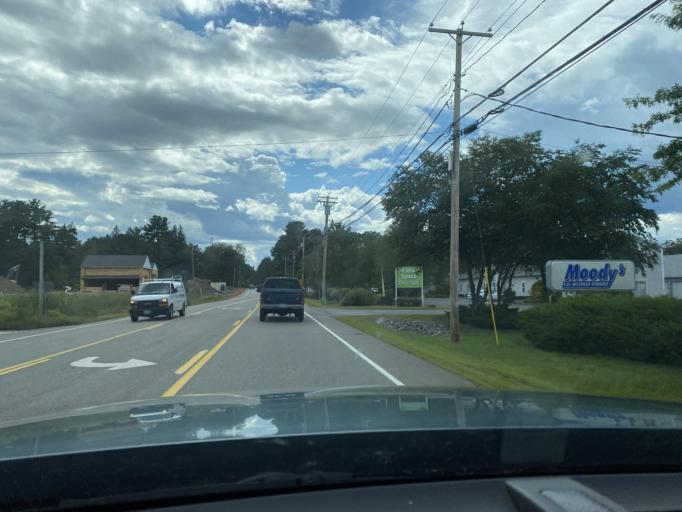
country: US
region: Maine
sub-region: York County
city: York Harbor
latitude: 43.1466
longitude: -70.6771
